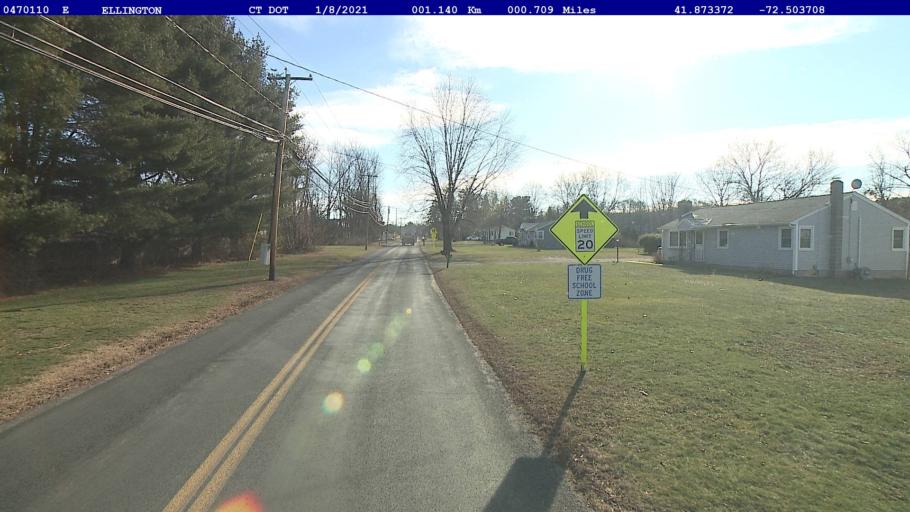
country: US
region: Connecticut
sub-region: Tolland County
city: Ellington
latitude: 41.8734
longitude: -72.5037
